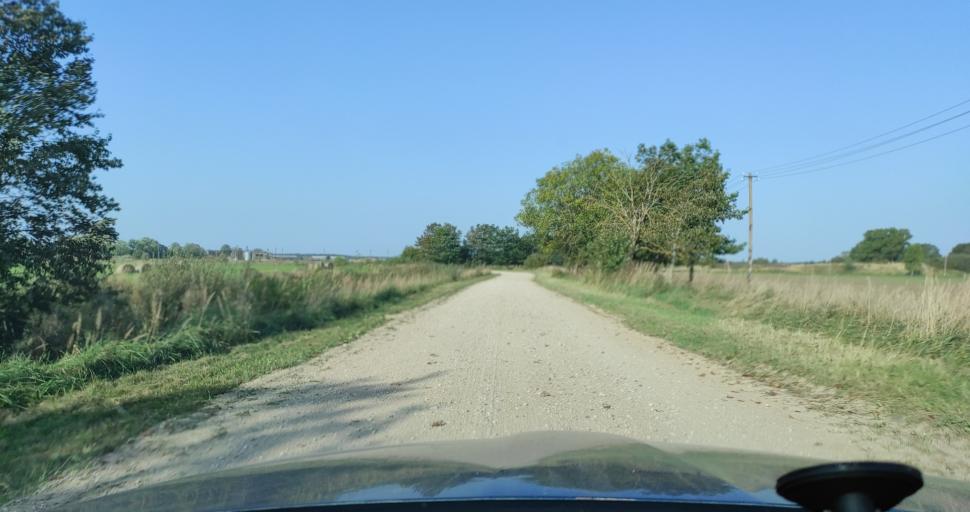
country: LV
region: Ventspils Rajons
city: Piltene
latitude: 57.2321
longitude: 21.6108
